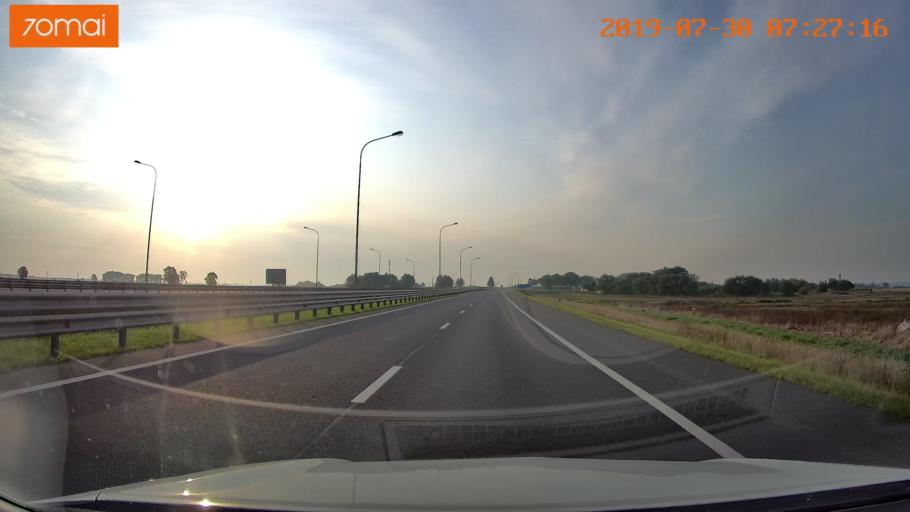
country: RU
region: Kaliningrad
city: Gvardeysk
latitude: 54.6831
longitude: 20.8827
